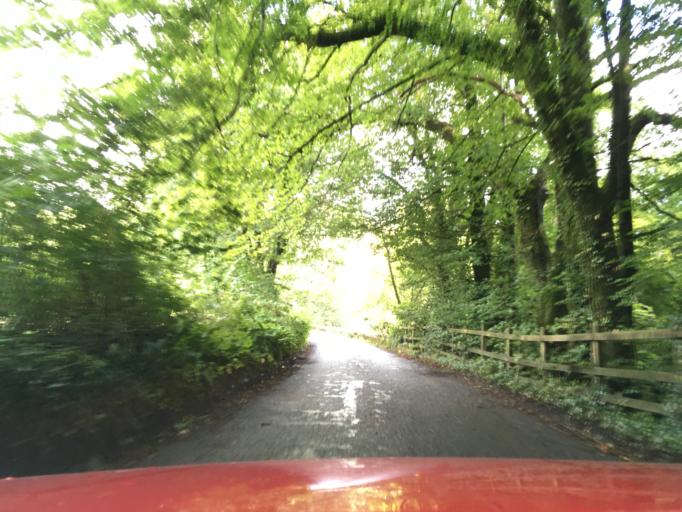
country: GB
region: England
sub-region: Devon
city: South Brent
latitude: 50.3991
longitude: -3.7963
